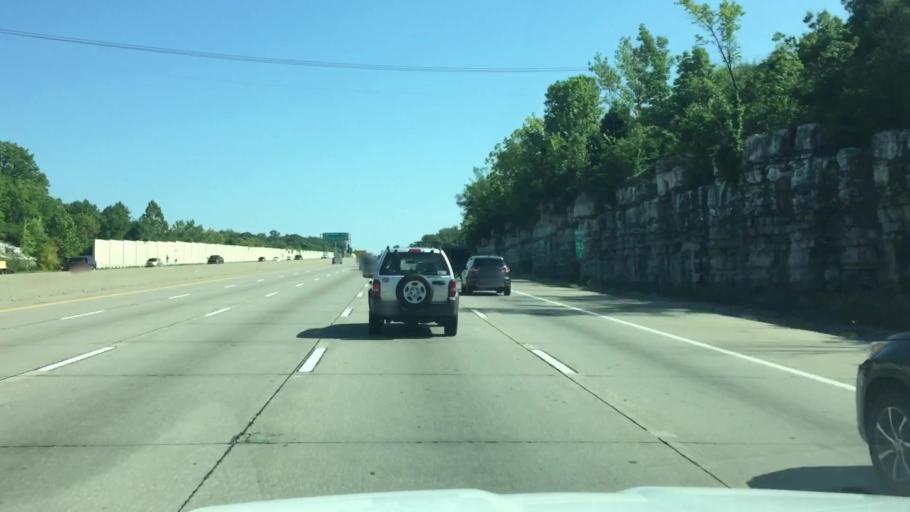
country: US
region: Missouri
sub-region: Jefferson County
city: Arnold
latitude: 38.4724
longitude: -90.3663
